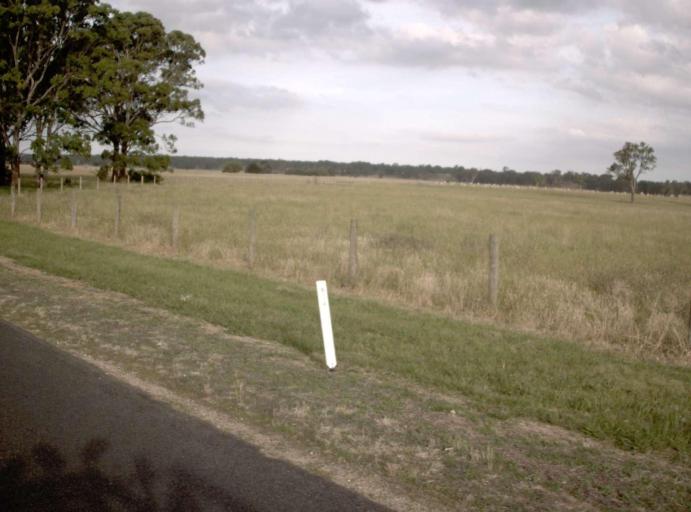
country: AU
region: Victoria
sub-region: Wellington
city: Sale
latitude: -37.8586
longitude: 147.0394
